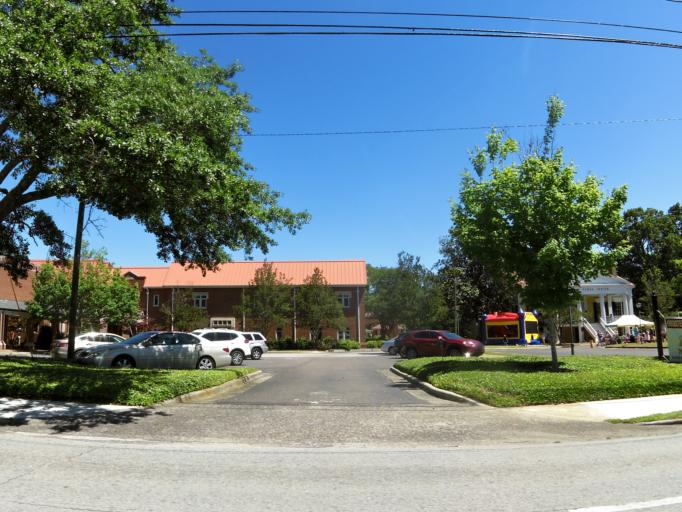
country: US
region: Georgia
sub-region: Richmond County
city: Augusta
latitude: 33.4776
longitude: -82.0159
